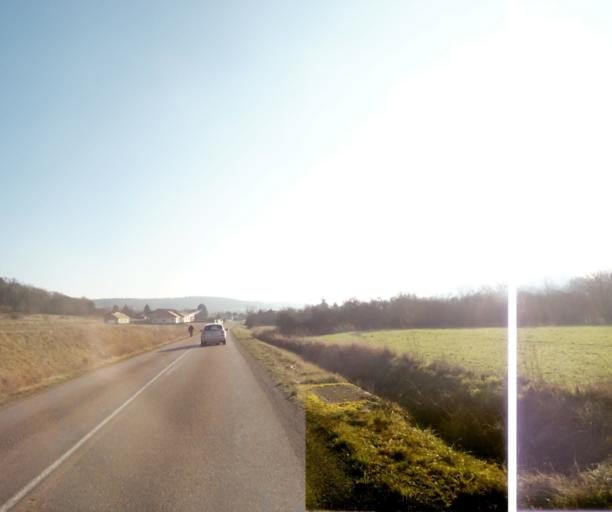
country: FR
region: Champagne-Ardenne
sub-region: Departement de la Haute-Marne
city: Chevillon
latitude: 48.4969
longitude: 5.1334
